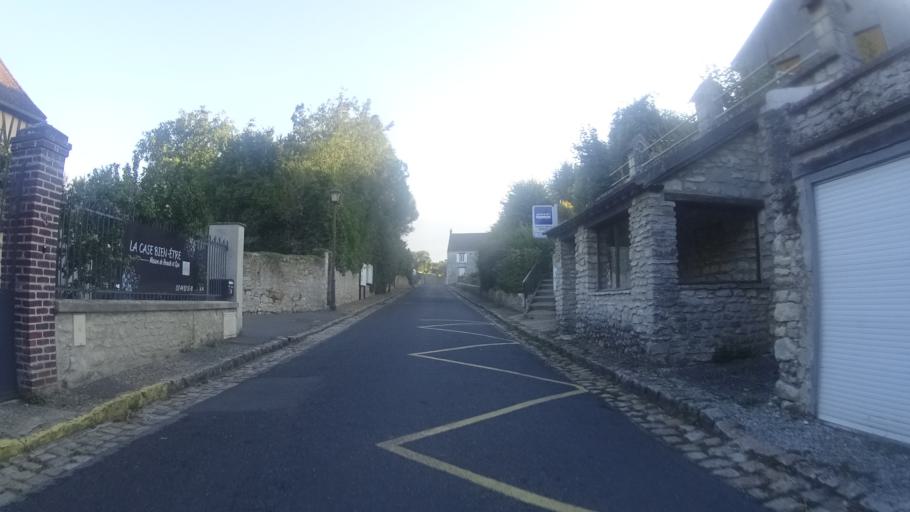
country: FR
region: Picardie
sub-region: Departement de l'Oise
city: Chamant
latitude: 49.1801
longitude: 2.6712
